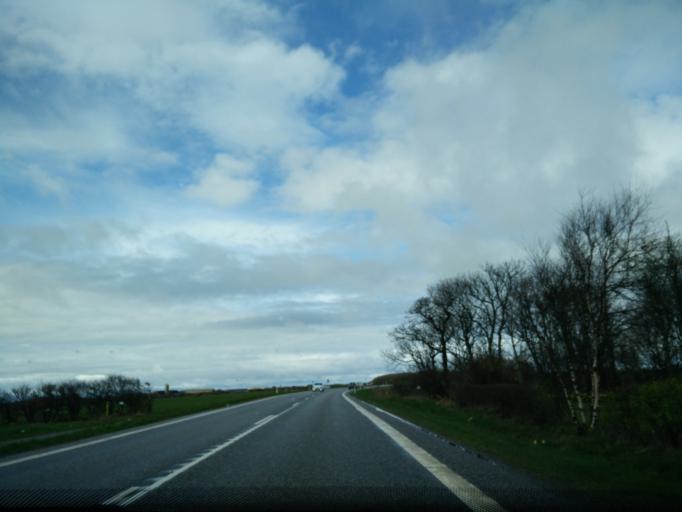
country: DK
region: Central Jutland
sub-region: Ringkobing-Skjern Kommune
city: Ringkobing
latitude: 56.1140
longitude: 8.1786
